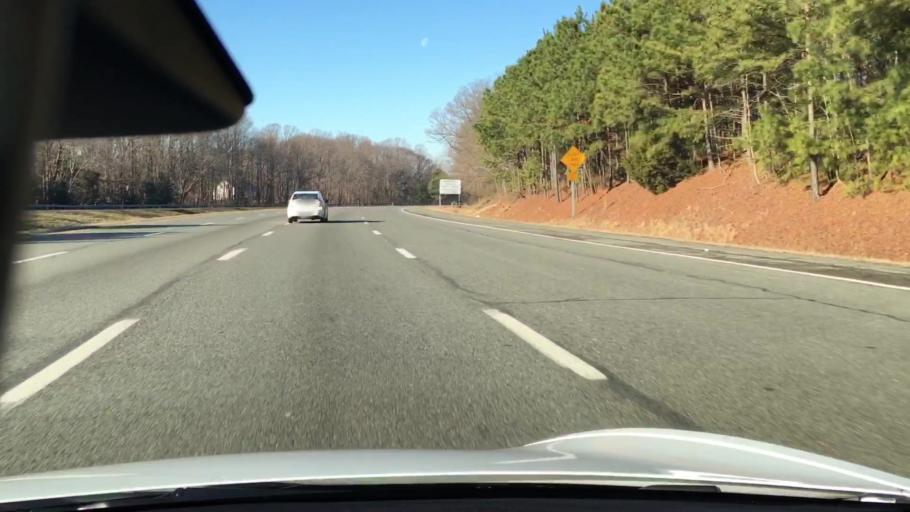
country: US
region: Virginia
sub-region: Henrico County
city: Montrose
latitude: 37.5301
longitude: -77.3681
